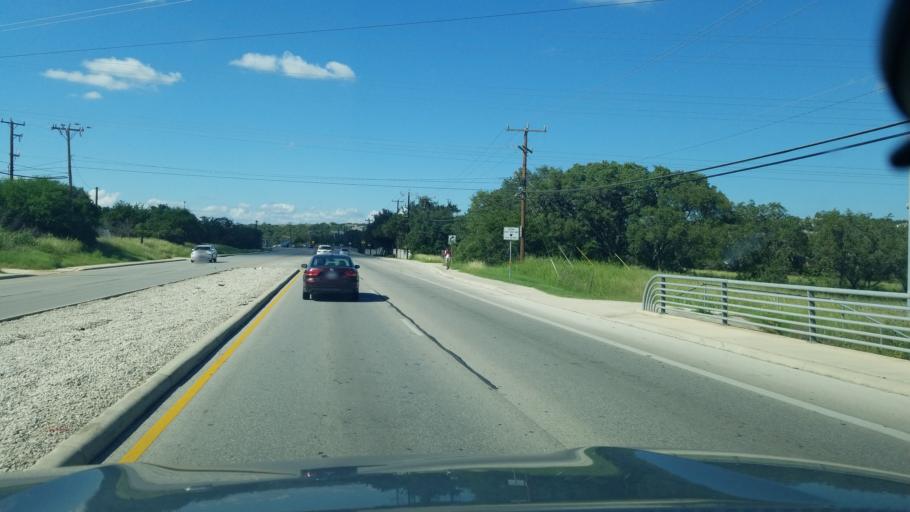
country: US
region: Texas
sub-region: Bexar County
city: Hollywood Park
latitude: 29.6178
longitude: -98.5105
